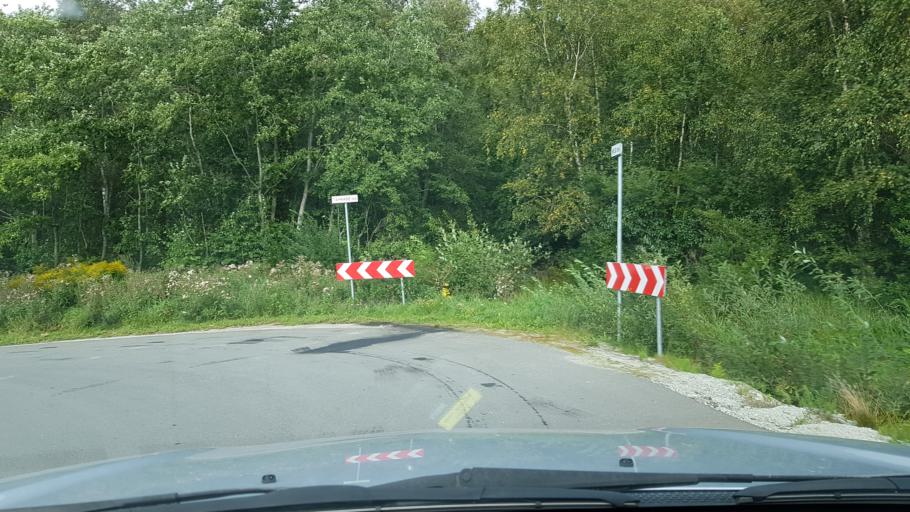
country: EE
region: Harju
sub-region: Tallinna linn
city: Kose
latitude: 59.3993
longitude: 24.8292
